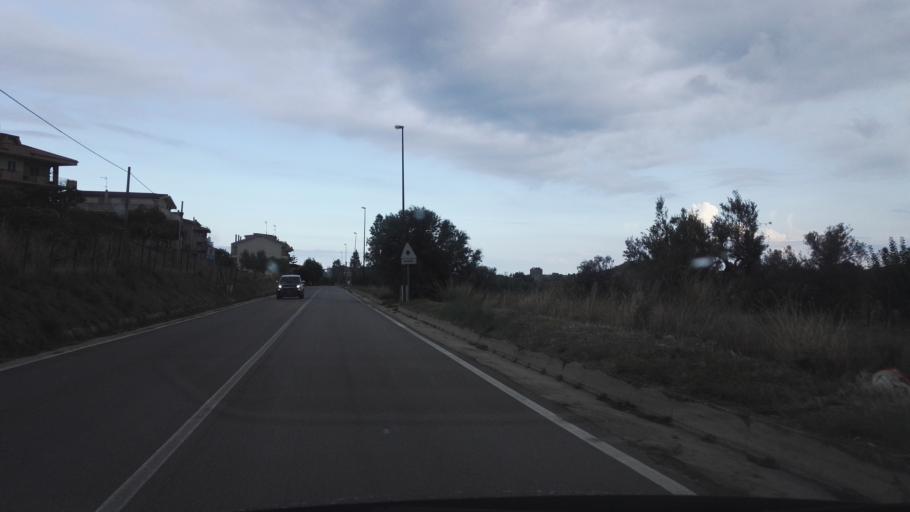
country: IT
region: Calabria
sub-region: Provincia di Catanzaro
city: Badolato Marina
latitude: 38.5732
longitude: 16.5577
